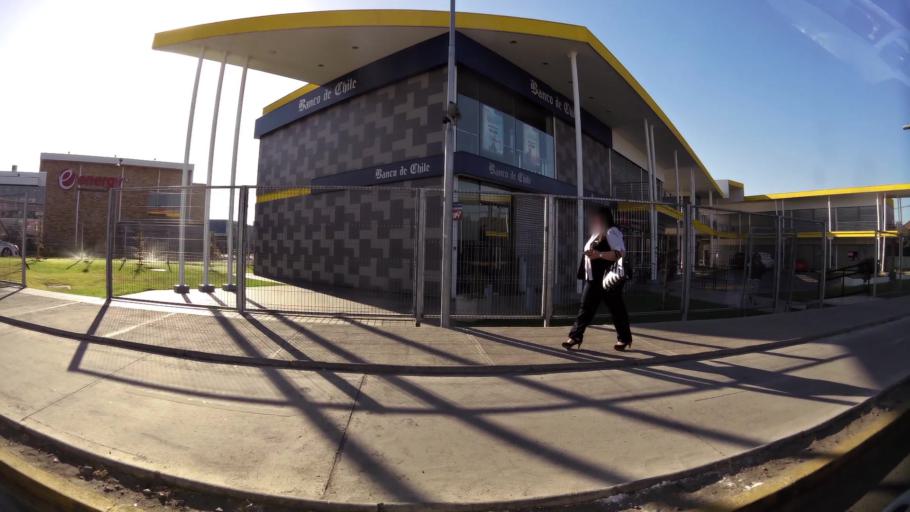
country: CL
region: Maule
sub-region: Provincia de Talca
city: Talca
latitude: -35.4435
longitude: -71.6865
